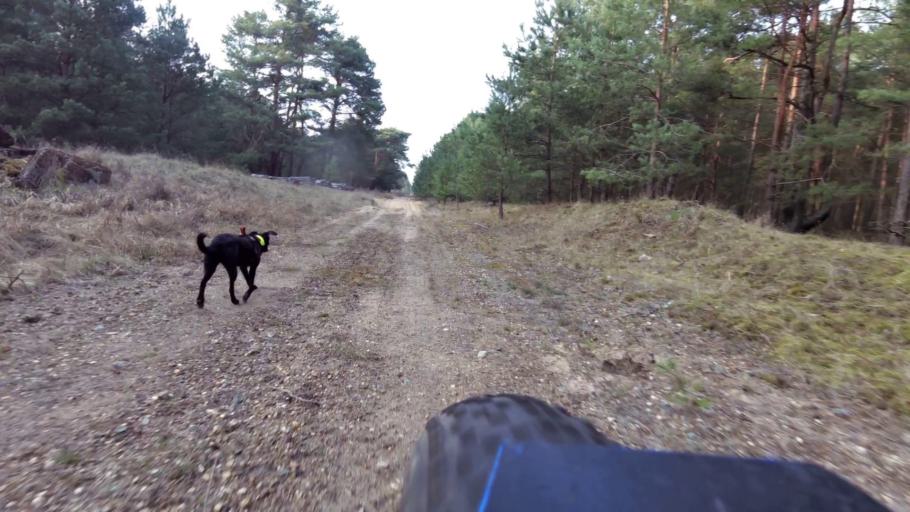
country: DE
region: Brandenburg
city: Vogelsang
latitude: 52.2649
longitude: 14.6919
